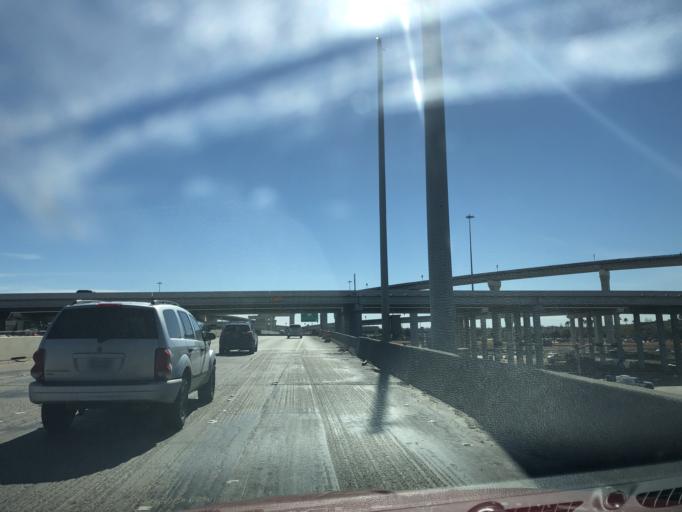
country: US
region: Texas
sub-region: Brazoria County
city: Brookside Village
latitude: 29.5987
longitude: -95.3869
